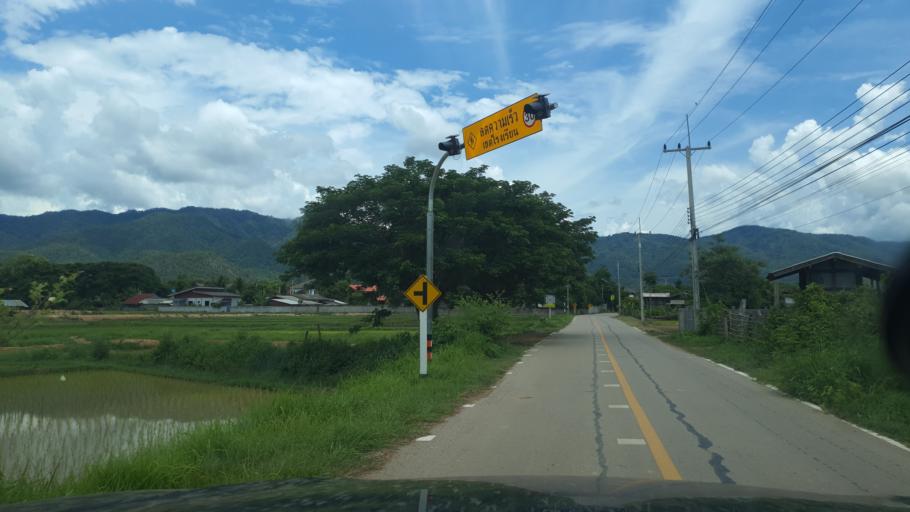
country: TH
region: Lampang
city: Sop Prap
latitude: 17.9103
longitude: 99.4134
